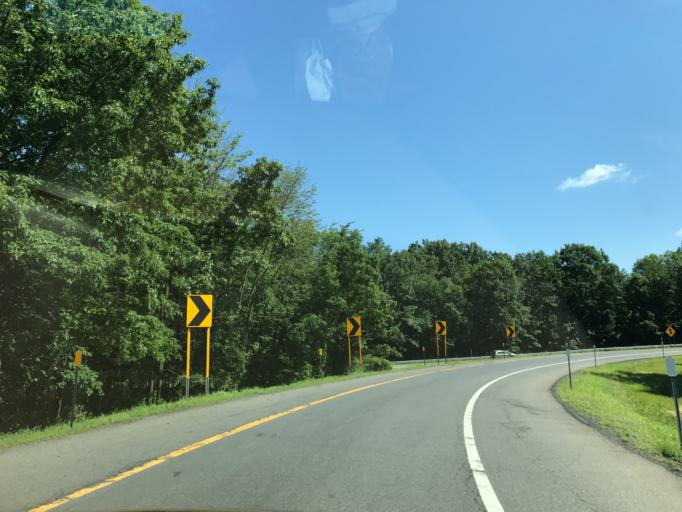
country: US
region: New York
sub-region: Columbia County
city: Niverville
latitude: 42.4807
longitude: -73.6726
